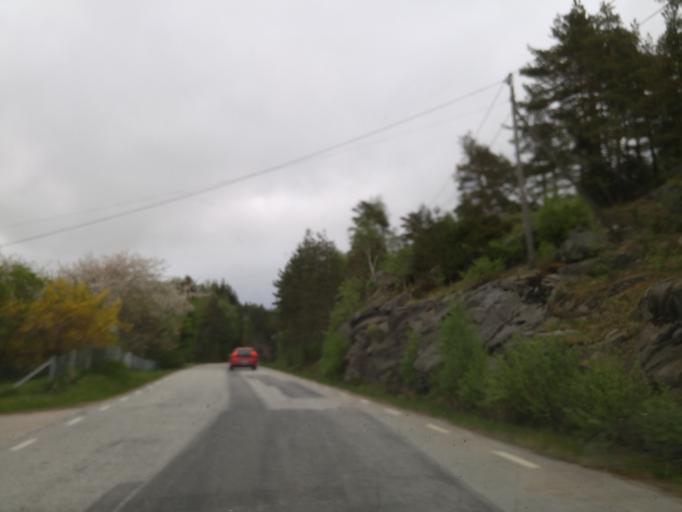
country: SE
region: Vaestra Goetaland
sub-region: Stenungsunds Kommun
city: Stora Hoga
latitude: 57.9934
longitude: 11.8381
